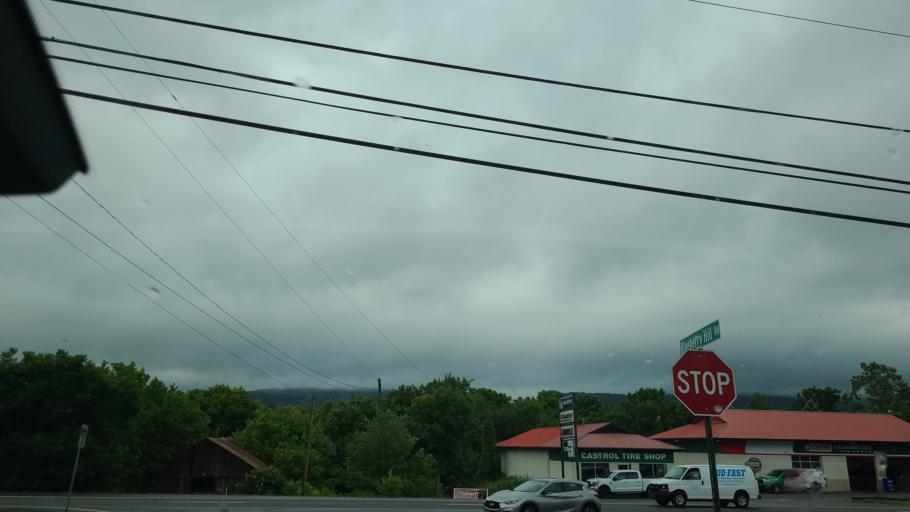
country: US
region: Tennessee
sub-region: Rhea County
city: Dayton
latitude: 35.5060
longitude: -85.0010
